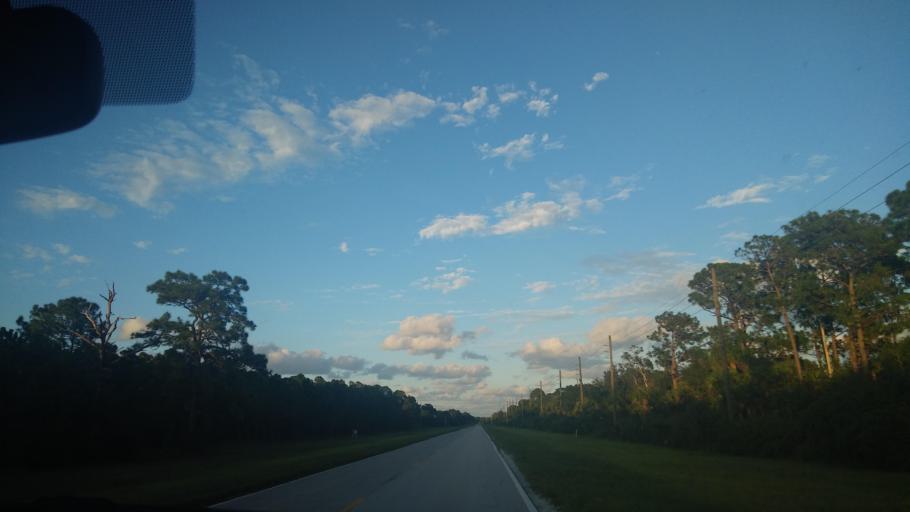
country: US
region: Florida
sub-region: Indian River County
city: Fellsmere
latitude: 27.7551
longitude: -80.6217
